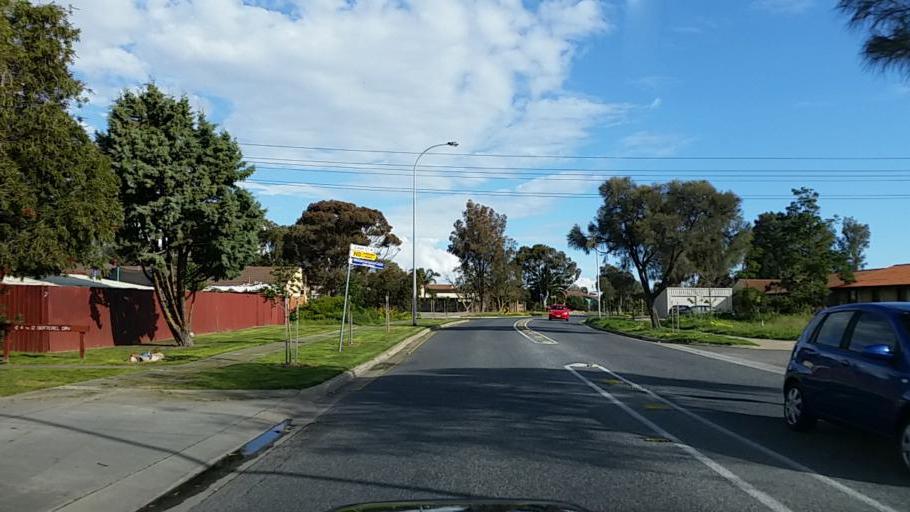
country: AU
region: South Australia
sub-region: Charles Sturt
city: West Lakes Shore
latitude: -34.8568
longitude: 138.4939
